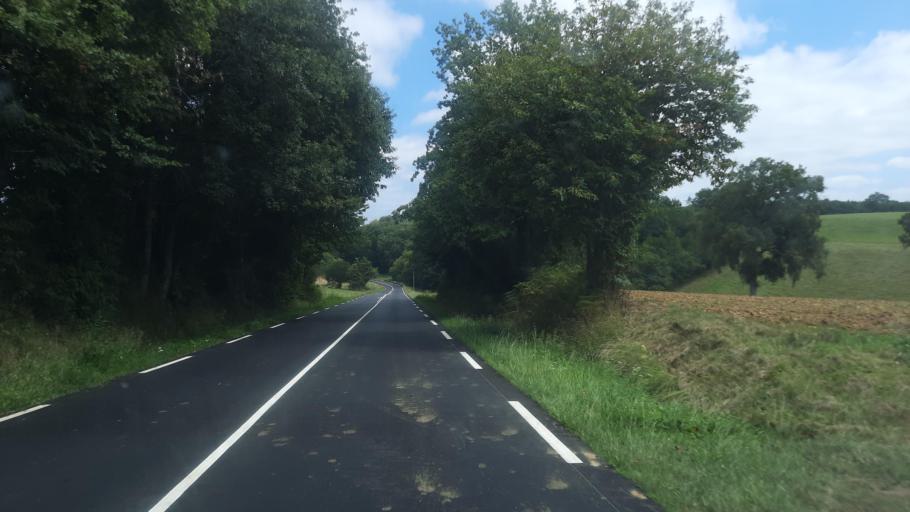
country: FR
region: Midi-Pyrenees
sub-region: Departement de la Haute-Garonne
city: Boulogne-sur-Gesse
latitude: 43.2921
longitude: 0.5713
